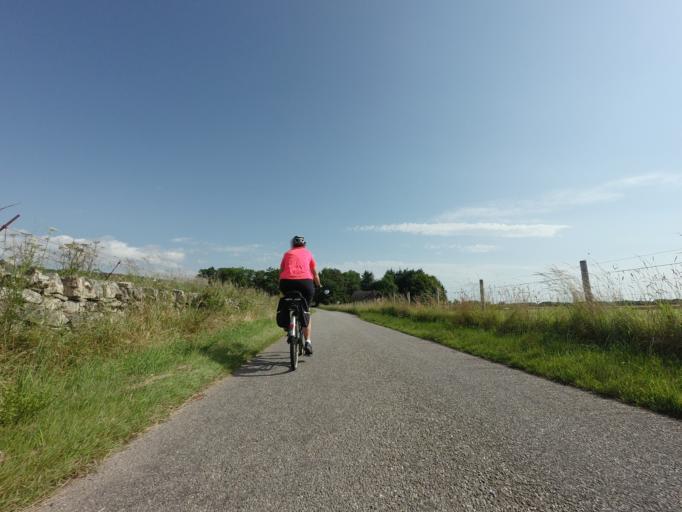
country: GB
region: Scotland
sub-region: Highland
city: Alness
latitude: 57.7115
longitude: -4.2235
